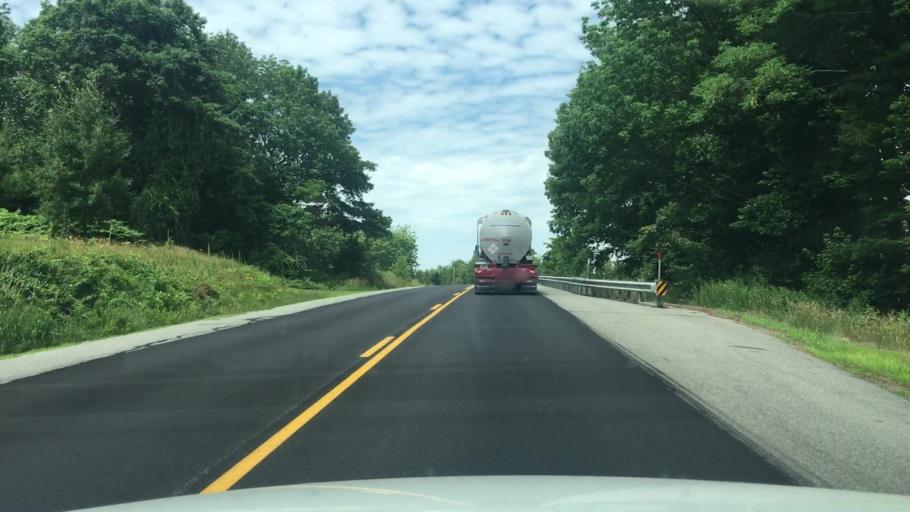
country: US
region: Maine
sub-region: Waldo County
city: Searsmont
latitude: 44.4067
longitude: -69.3037
